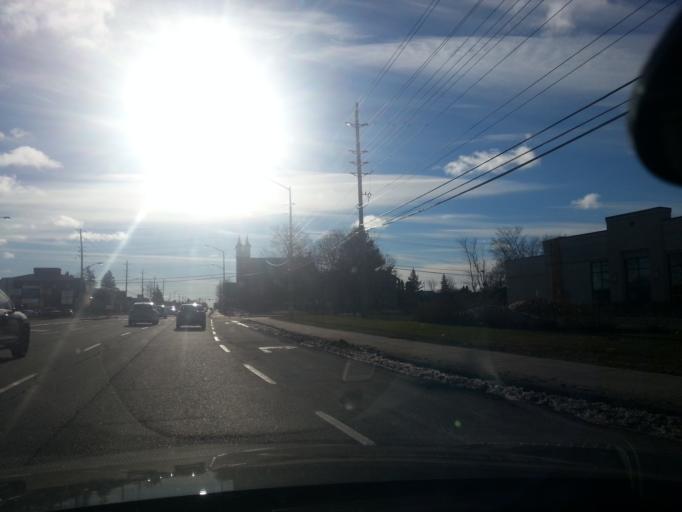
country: CA
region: Ontario
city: Ottawa
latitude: 45.3341
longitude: -75.7238
